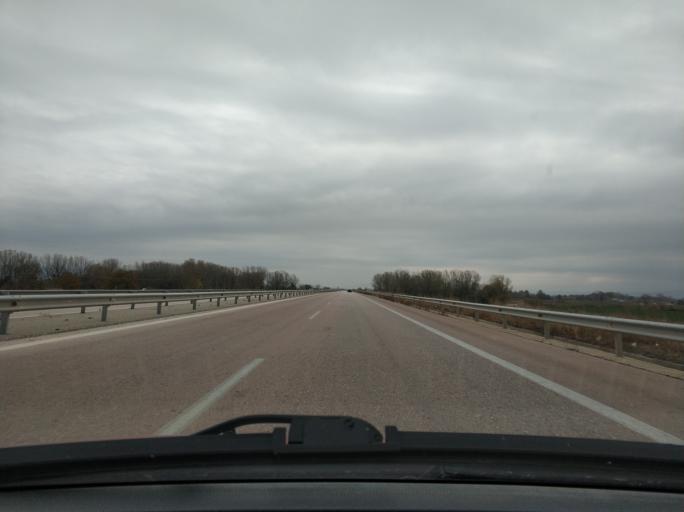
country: GR
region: Central Macedonia
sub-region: Nomos Thessalonikis
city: Kavallari
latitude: 40.7305
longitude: 23.0573
